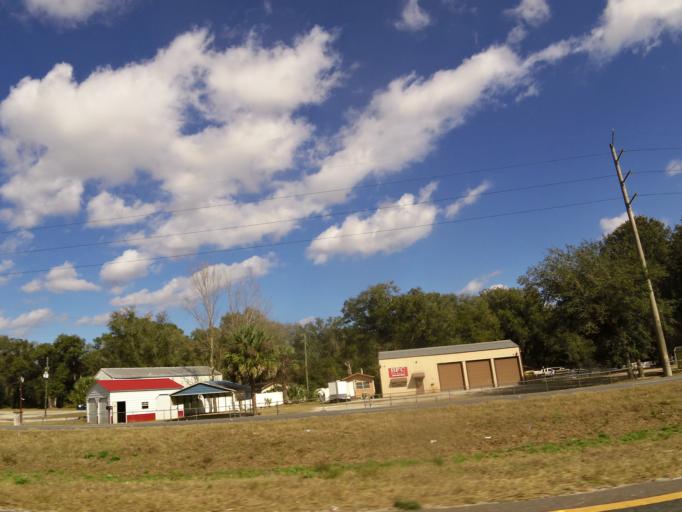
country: US
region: Florida
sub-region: Volusia County
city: De Leon Springs
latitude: 29.0932
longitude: -81.3309
